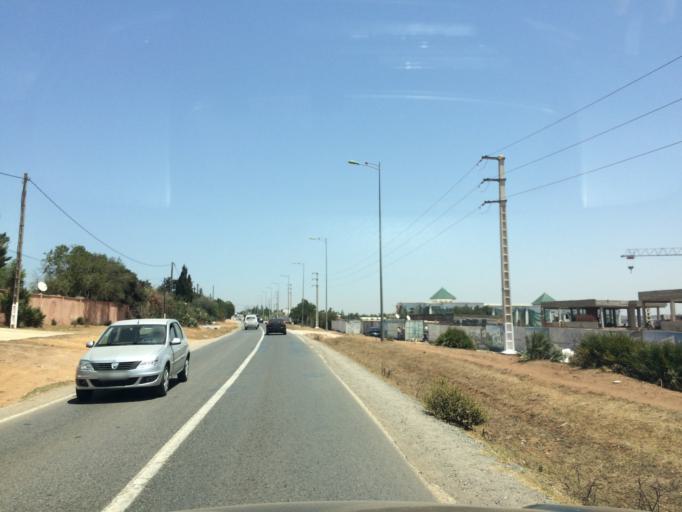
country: MA
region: Rabat-Sale-Zemmour-Zaer
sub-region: Skhirate-Temara
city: Temara
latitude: 33.8923
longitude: -6.8345
